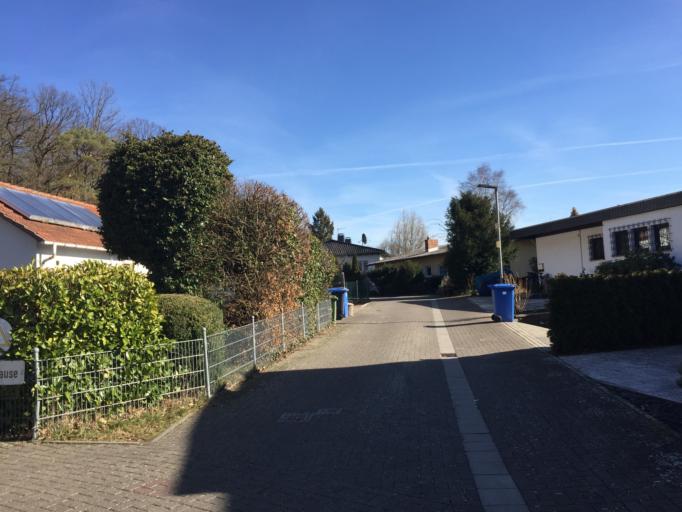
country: DE
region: Hesse
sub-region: Regierungsbezirk Giessen
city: Langgons
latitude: 50.5386
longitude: 8.6823
